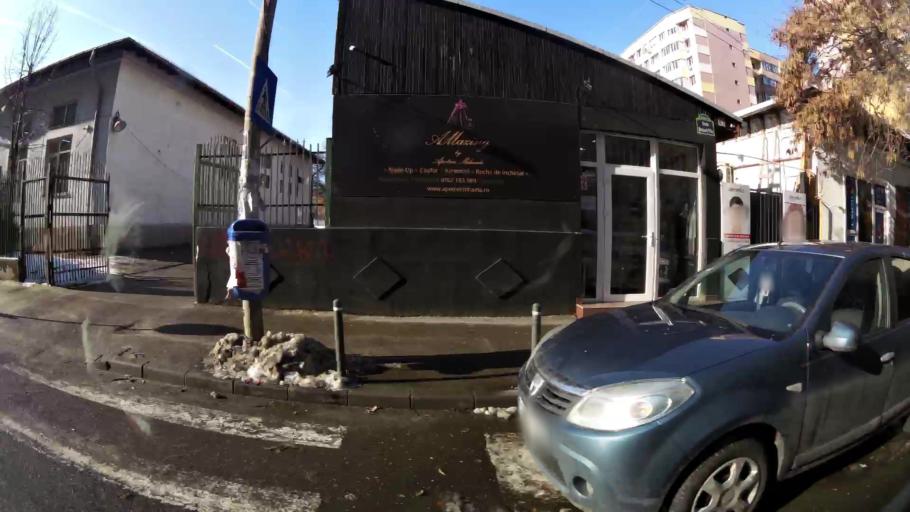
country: RO
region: Bucuresti
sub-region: Municipiul Bucuresti
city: Bucharest
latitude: 44.4569
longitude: 26.1274
